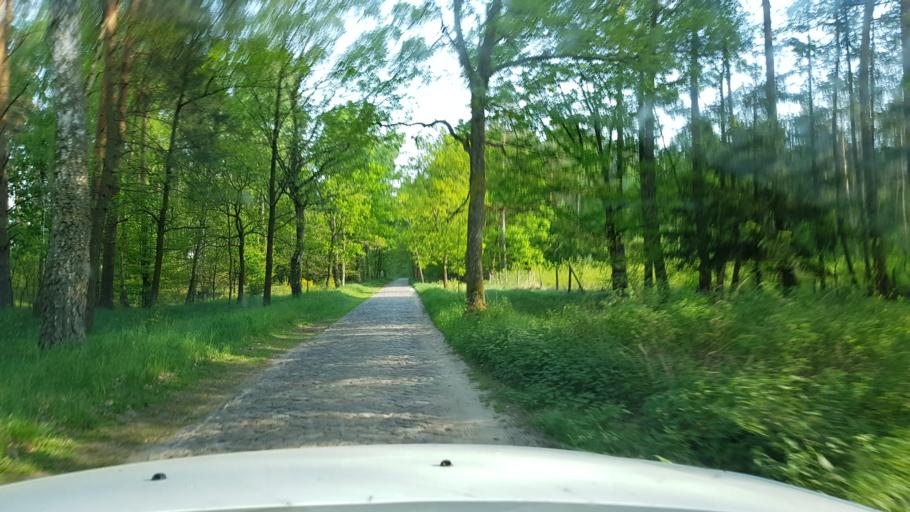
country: PL
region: West Pomeranian Voivodeship
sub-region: Powiat lobeski
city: Resko
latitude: 53.7208
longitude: 15.3291
